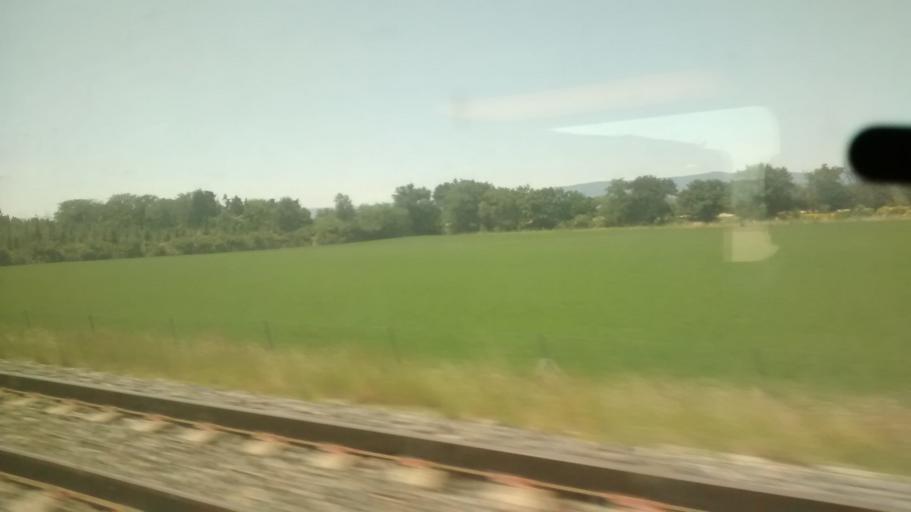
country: FR
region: Rhone-Alpes
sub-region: Departement de la Drome
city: Sauzet
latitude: 44.5864
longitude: 4.8579
